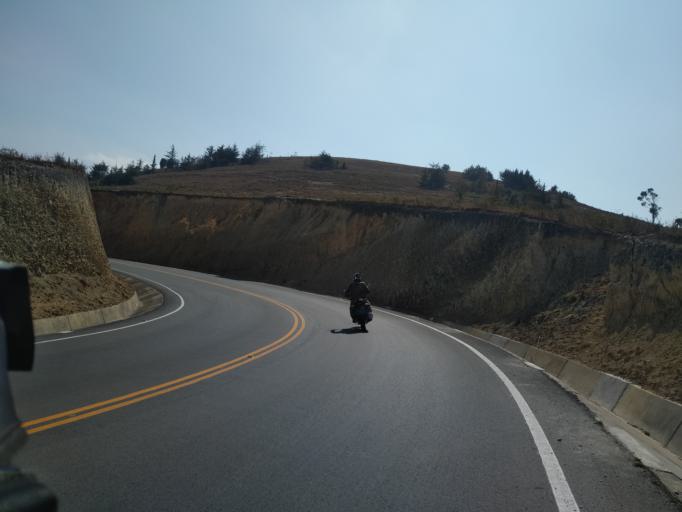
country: PE
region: Cajamarca
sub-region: Provincia de Cajamarca
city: Llacanora
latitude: -7.2117
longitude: -78.3941
